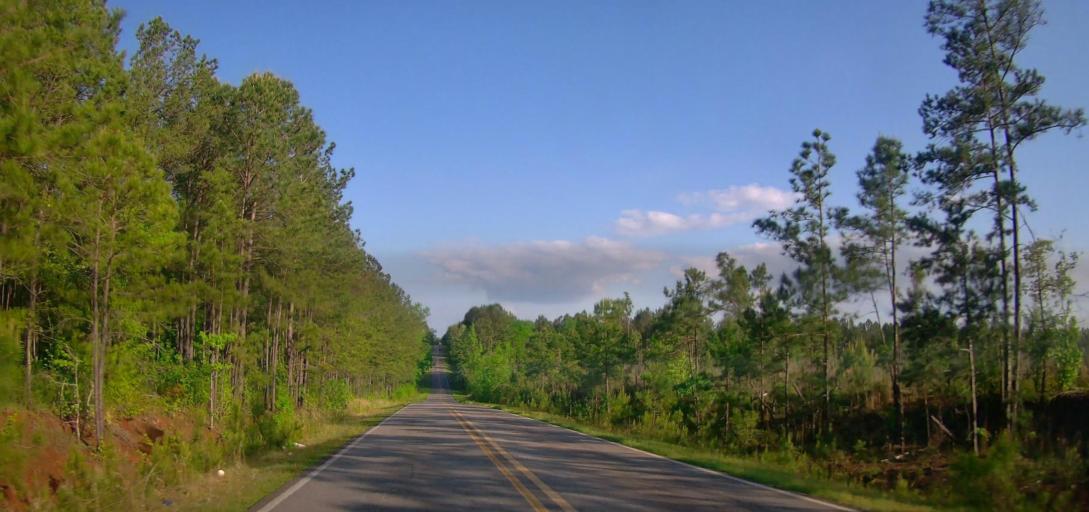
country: US
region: Georgia
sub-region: Putnam County
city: Eatonton
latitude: 33.2803
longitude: -83.3150
